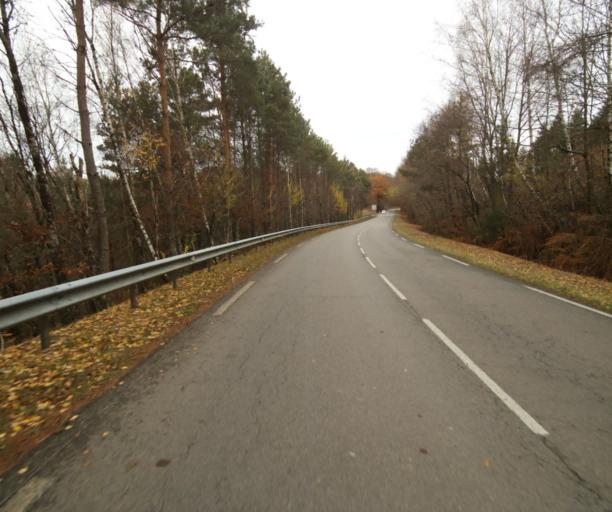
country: FR
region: Limousin
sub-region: Departement de la Correze
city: Sainte-Fortunade
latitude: 45.1830
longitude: 1.7605
